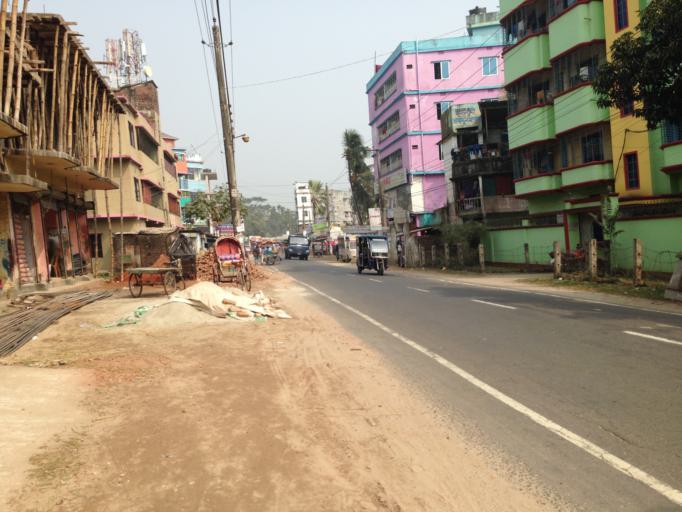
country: BD
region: Chittagong
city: Lakshmipur
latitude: 22.9350
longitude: 90.8374
